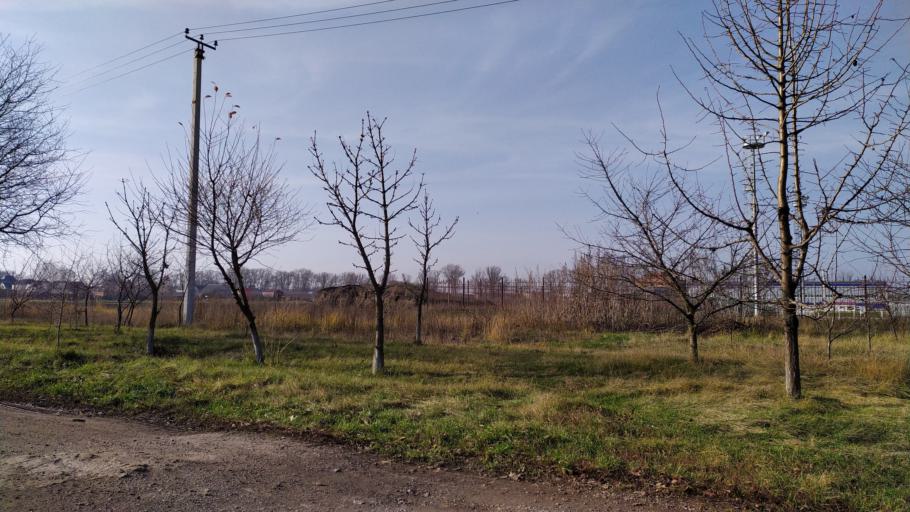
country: RU
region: Kursk
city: Kursk
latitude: 51.6408
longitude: 36.1307
